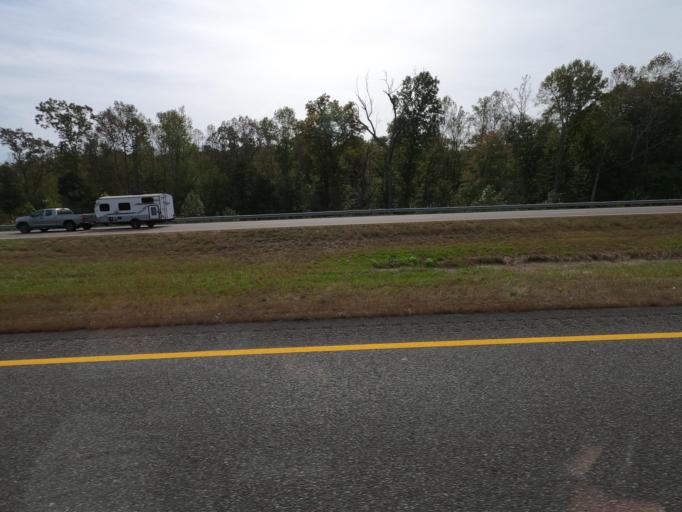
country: US
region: Tennessee
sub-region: Decatur County
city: Parsons
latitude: 35.8155
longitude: -88.2017
